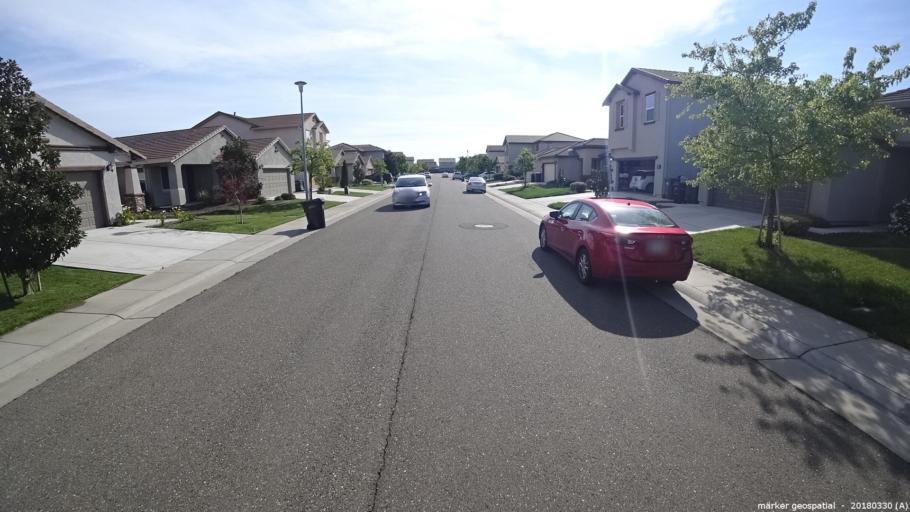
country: US
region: California
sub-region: Sacramento County
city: Vineyard
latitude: 38.4841
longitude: -121.3443
